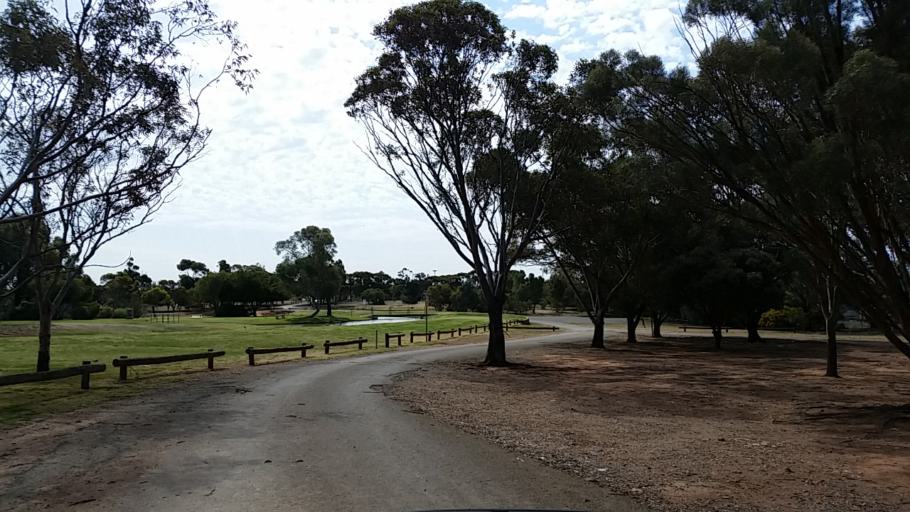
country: AU
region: South Australia
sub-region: Peterborough
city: Peterborough
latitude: -32.9803
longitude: 138.8349
